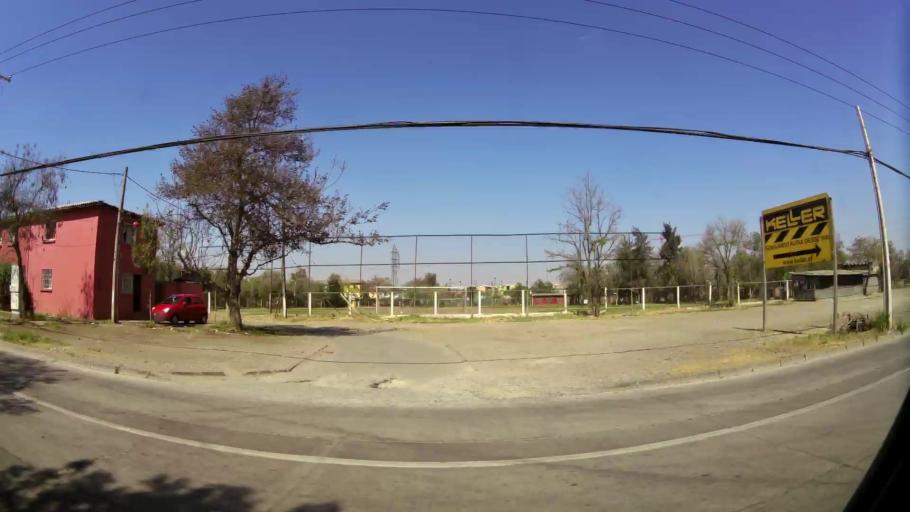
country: CL
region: Santiago Metropolitan
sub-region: Provincia de Santiago
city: Santiago
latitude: -33.4771
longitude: -70.6386
